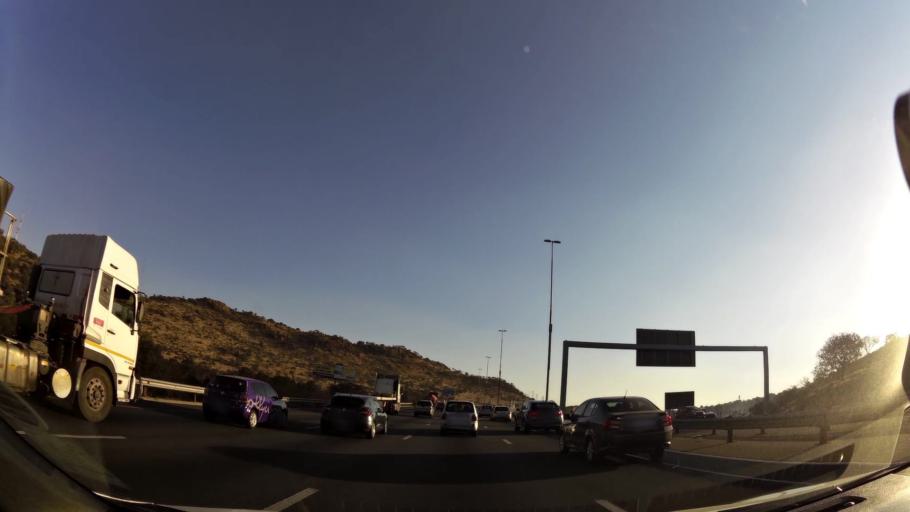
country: ZA
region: Gauteng
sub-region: City of Johannesburg Metropolitan Municipality
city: Johannesburg
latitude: -26.2652
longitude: 28.0767
